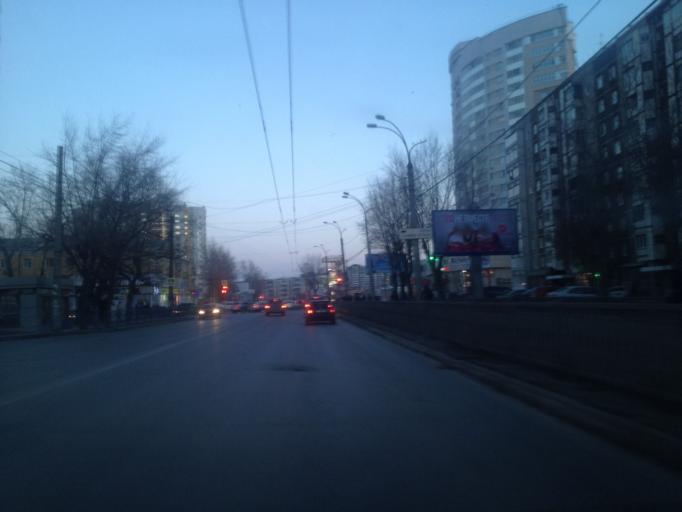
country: RU
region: Sverdlovsk
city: Yekaterinburg
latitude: 56.8015
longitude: 60.6293
